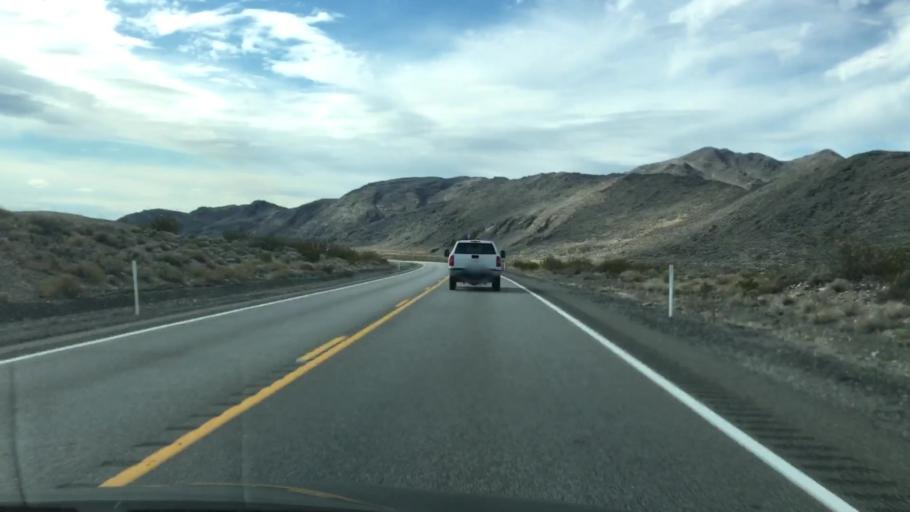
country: US
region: Nevada
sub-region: Nye County
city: Pahrump
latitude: 36.5881
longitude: -116.0520
